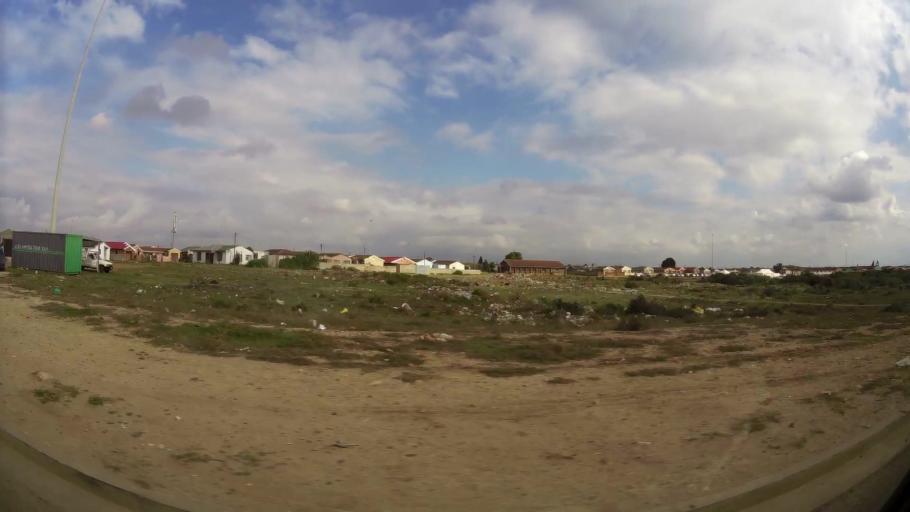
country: ZA
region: Eastern Cape
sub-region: Nelson Mandela Bay Metropolitan Municipality
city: Port Elizabeth
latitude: -33.8154
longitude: 25.5927
